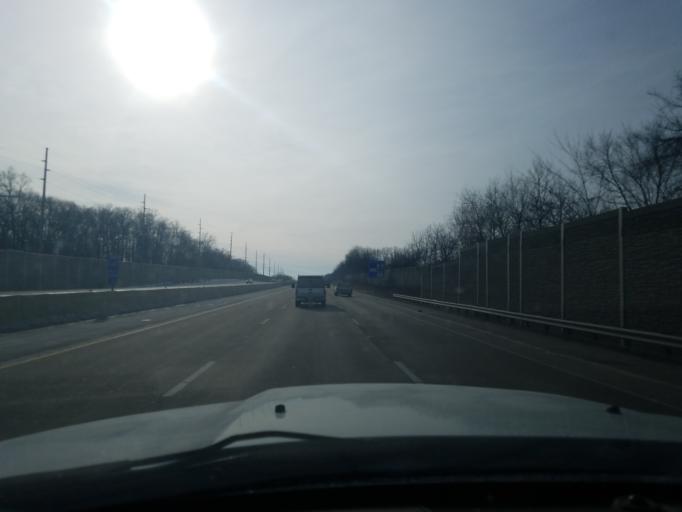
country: US
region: Indiana
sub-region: Allen County
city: Fort Wayne
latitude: 41.0594
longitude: -85.2408
